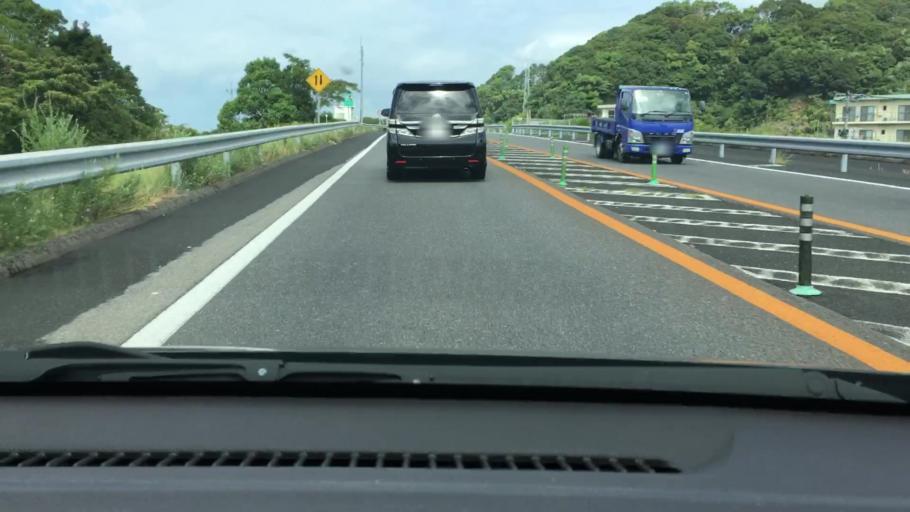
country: JP
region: Nagasaki
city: Sasebo
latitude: 33.1501
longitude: 129.7675
